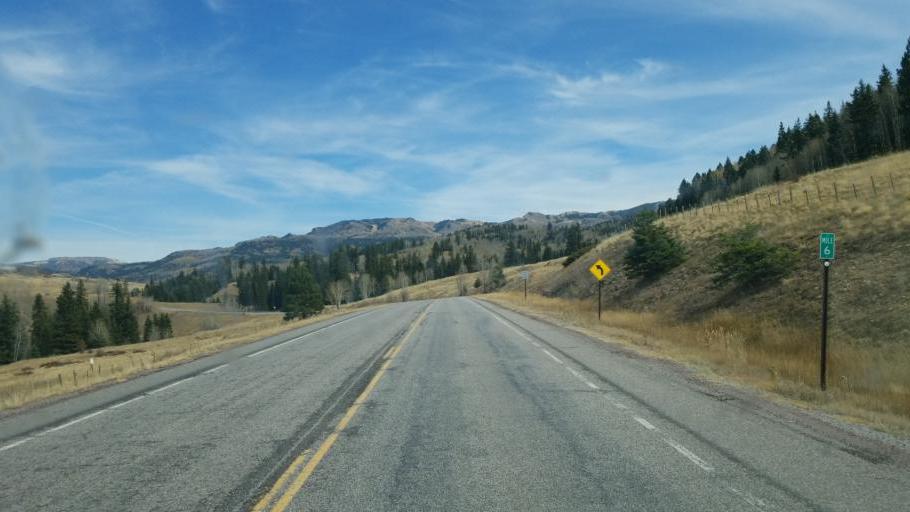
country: US
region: New Mexico
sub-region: Rio Arriba County
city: Chama
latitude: 36.9544
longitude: -106.5359
